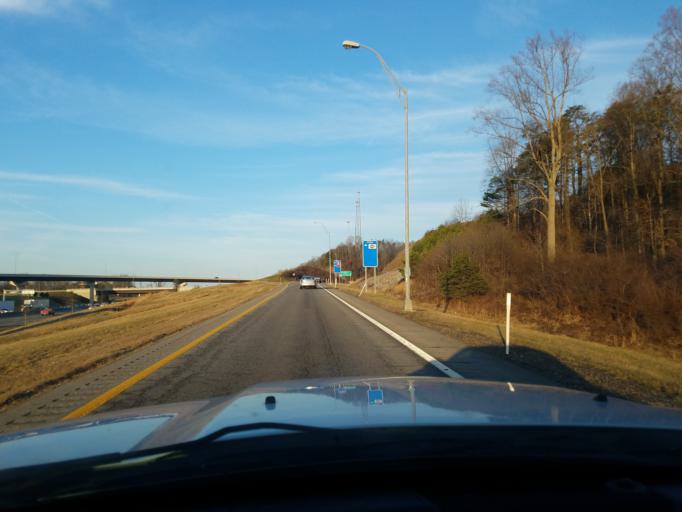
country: US
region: West Virginia
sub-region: Putnam County
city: Teays Valley
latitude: 38.4548
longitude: -81.8990
